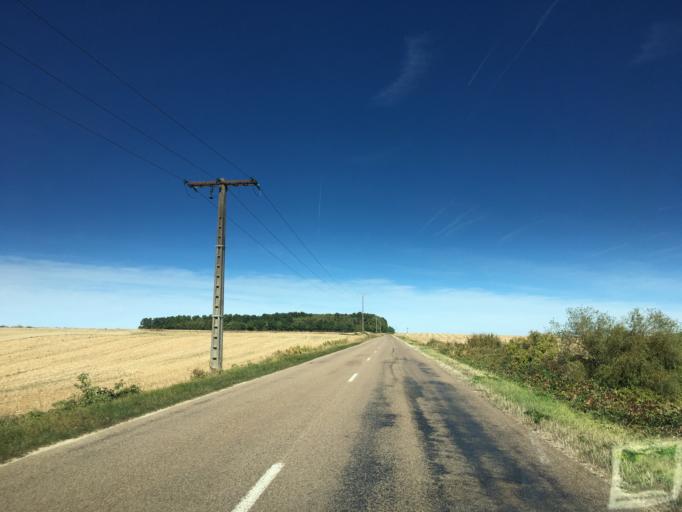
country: FR
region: Bourgogne
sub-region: Departement de l'Yonne
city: Vermenton
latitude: 47.6695
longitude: 3.6600
